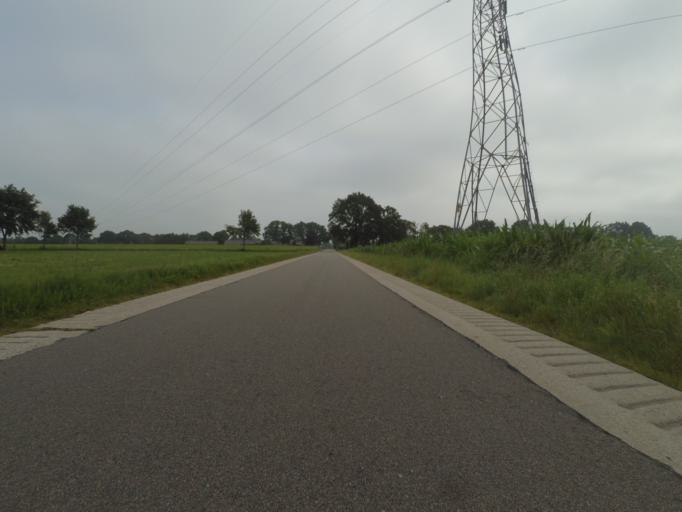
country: NL
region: Gelderland
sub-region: Gemeente Barneveld
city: Kootwijkerbroek
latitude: 52.1416
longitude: 5.6560
